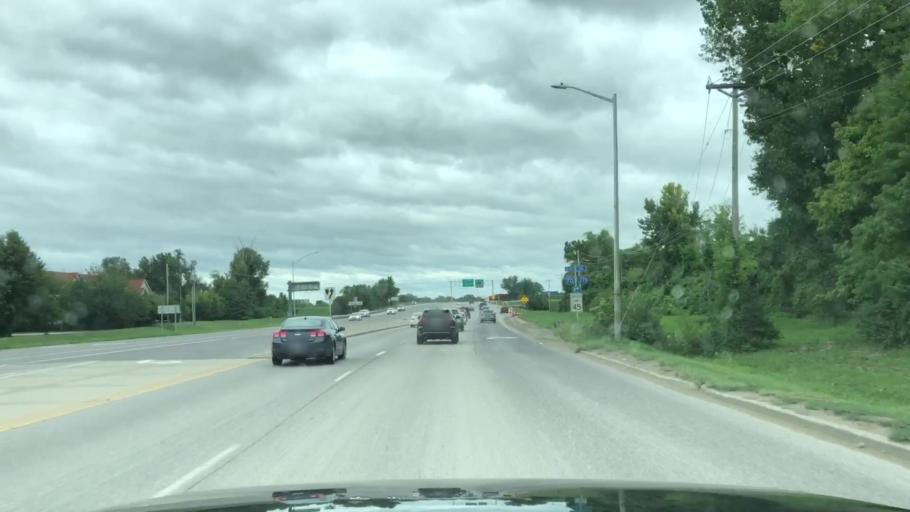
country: US
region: Missouri
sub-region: Saint Charles County
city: Saint Charles
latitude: 38.7495
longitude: -90.4624
